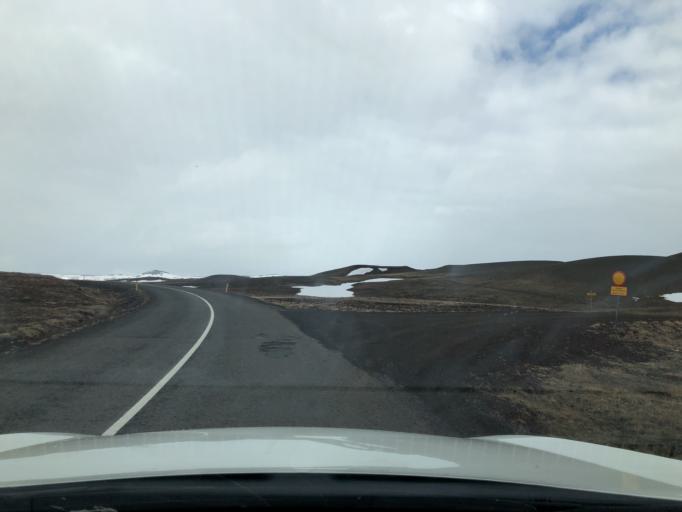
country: IS
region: Northeast
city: Laugar
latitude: 65.7139
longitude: -16.7628
